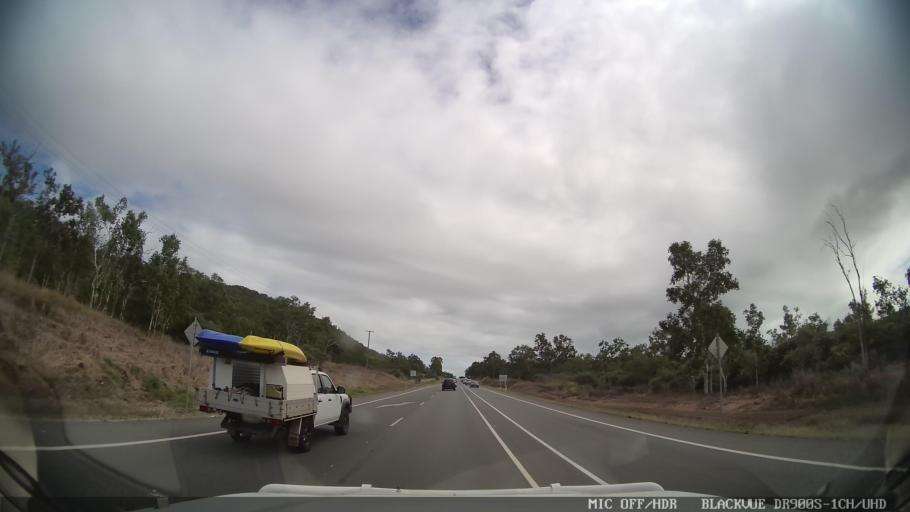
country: AU
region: Queensland
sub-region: Townsville
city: Townsville
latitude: -19.3681
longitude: 146.8936
